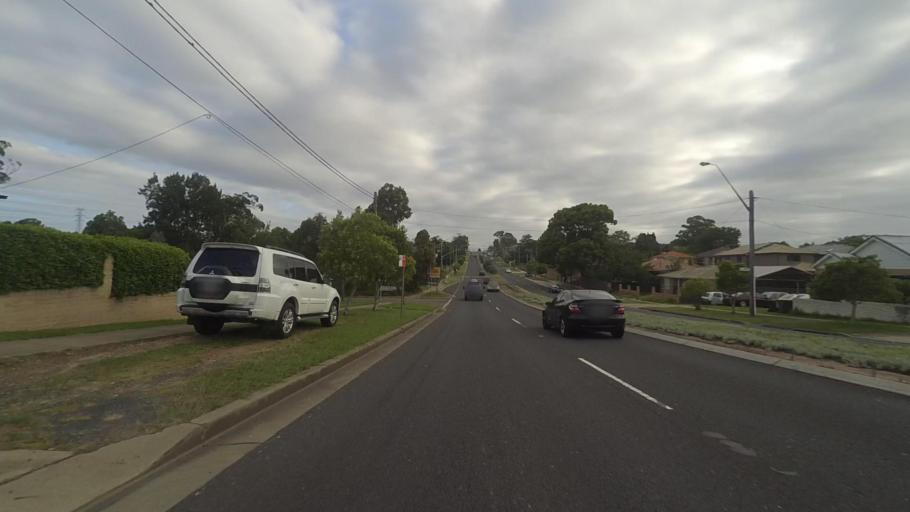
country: AU
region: New South Wales
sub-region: Bankstown
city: Padstow
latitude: -33.9554
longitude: 151.0381
